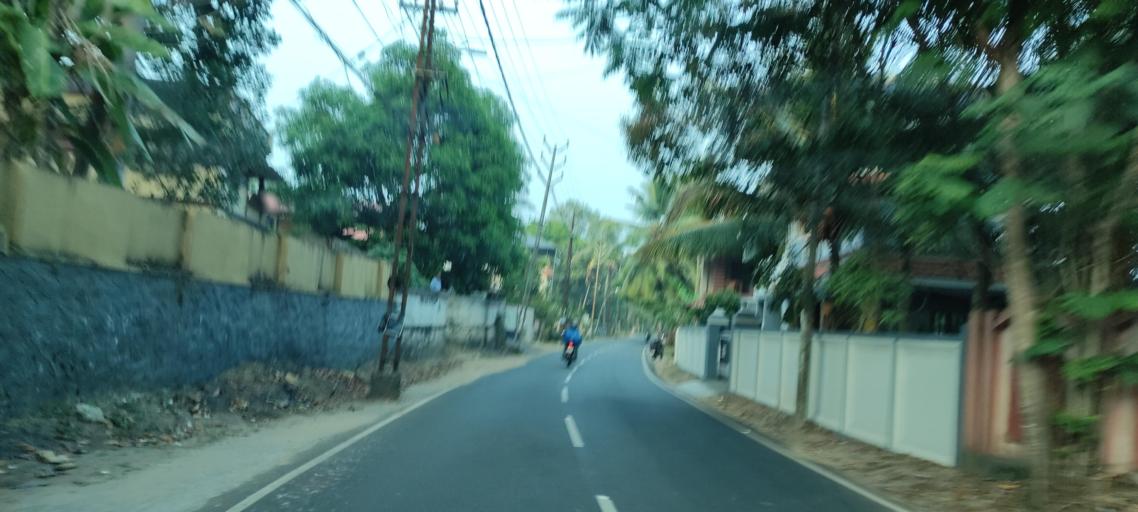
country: IN
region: Kerala
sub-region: Alappuzha
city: Mavelikara
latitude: 9.2586
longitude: 76.5538
